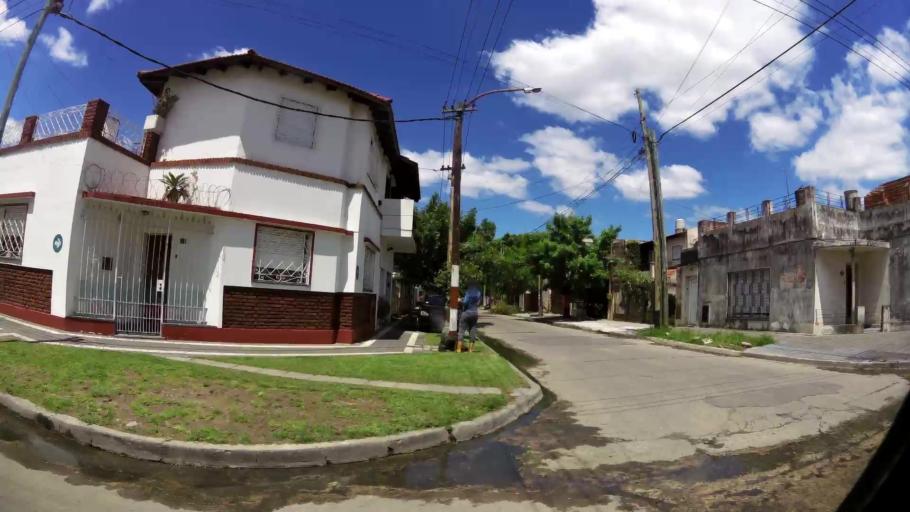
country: AR
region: Buenos Aires
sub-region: Partido de Lomas de Zamora
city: Lomas de Zamora
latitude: -34.7301
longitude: -58.4141
